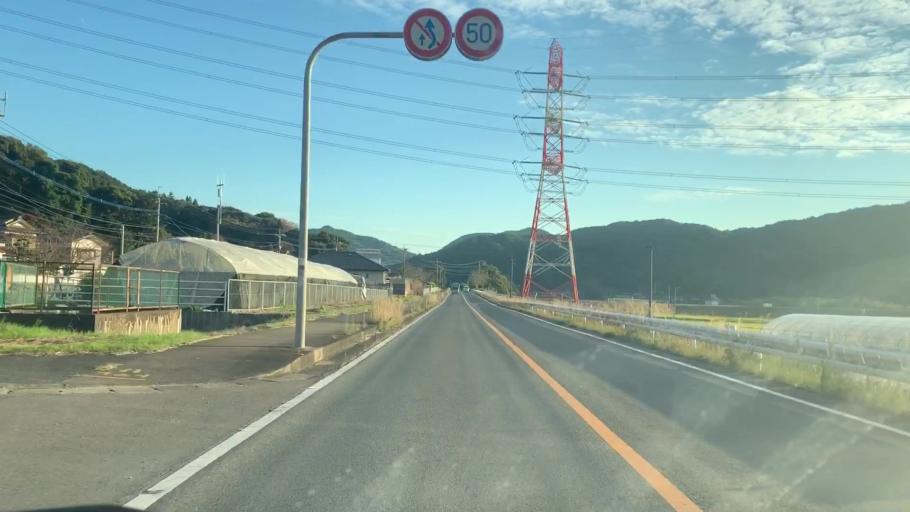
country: JP
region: Saga Prefecture
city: Karatsu
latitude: 33.3876
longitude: 129.9879
